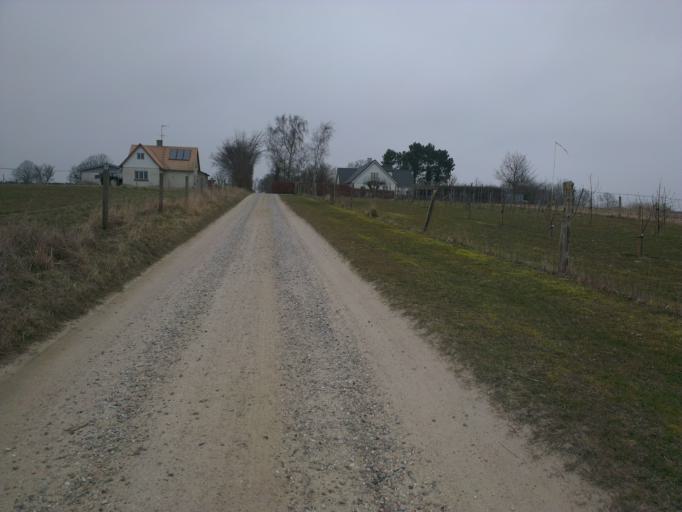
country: DK
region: Capital Region
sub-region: Frederikssund Kommune
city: Frederikssund
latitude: 55.7773
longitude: 12.0392
